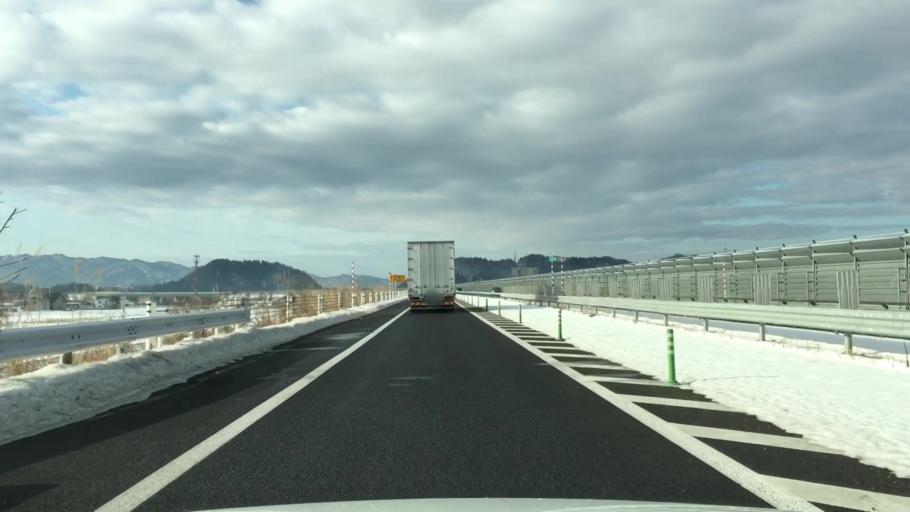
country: JP
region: Akita
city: Odate
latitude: 40.2905
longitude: 140.5479
